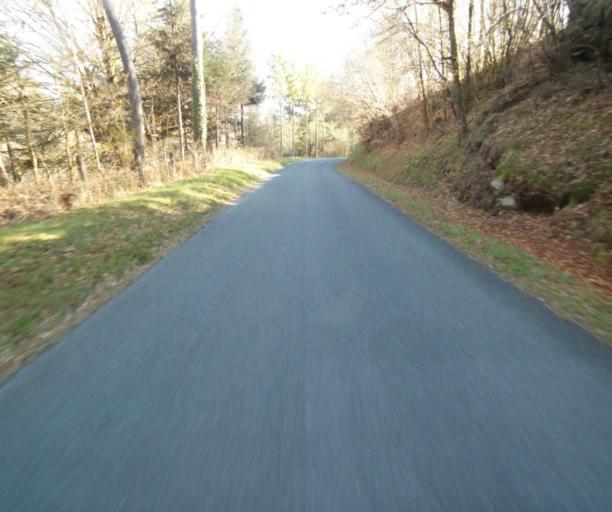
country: FR
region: Limousin
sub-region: Departement de la Correze
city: Correze
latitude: 45.3072
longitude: 1.8798
